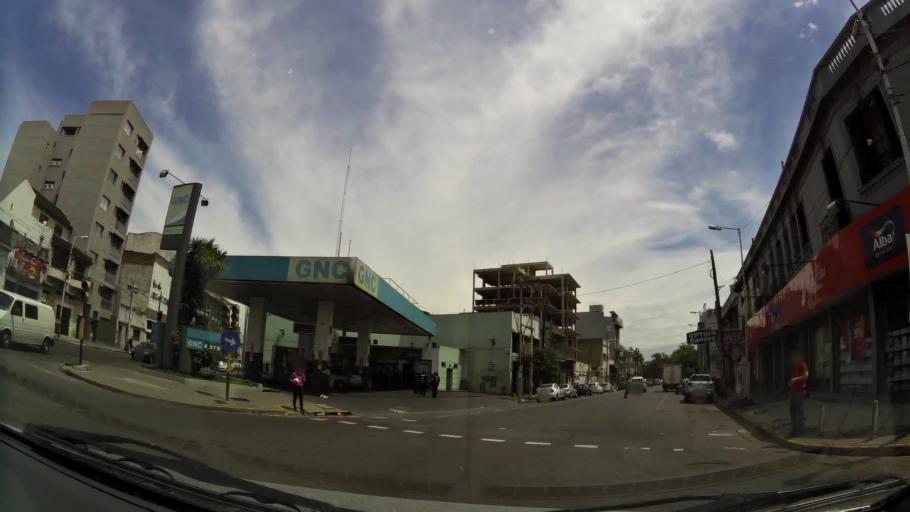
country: AR
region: Buenos Aires
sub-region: Partido de Avellaneda
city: Avellaneda
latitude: -34.6705
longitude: -58.3909
